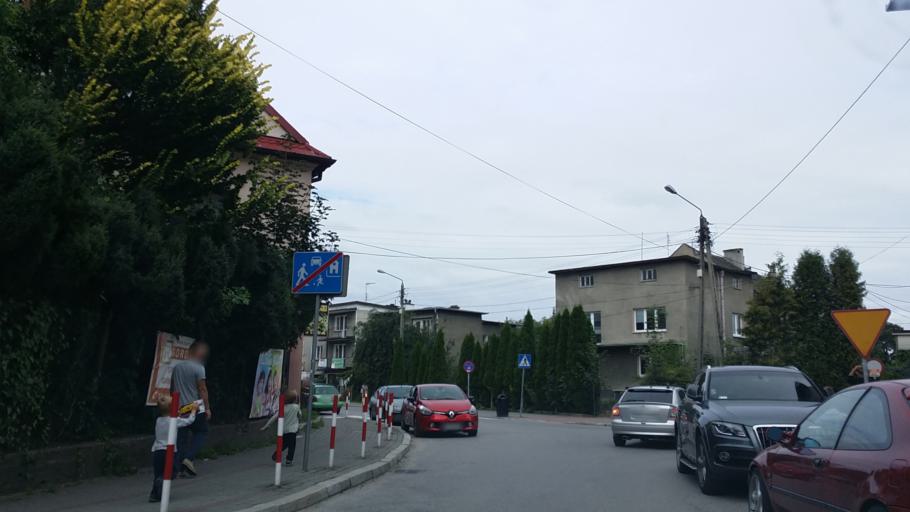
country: PL
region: Lesser Poland Voivodeship
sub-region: Powiat wadowicki
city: Wadowice
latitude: 49.8853
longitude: 19.4910
